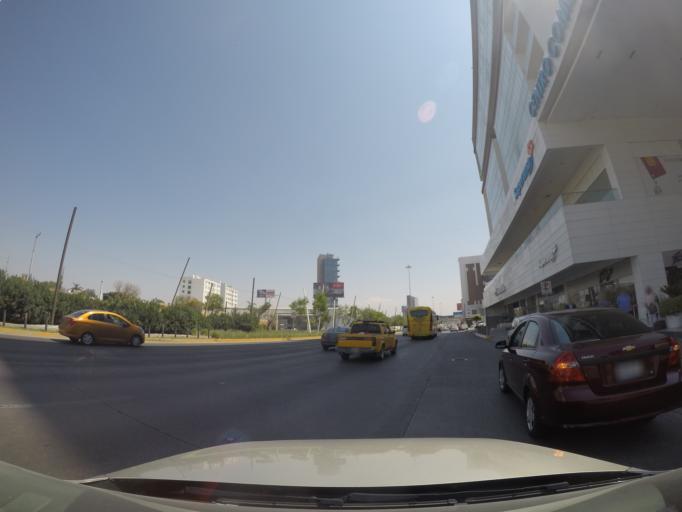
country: MX
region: Puebla
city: Tlazcalancingo
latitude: 19.0161
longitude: -98.2530
